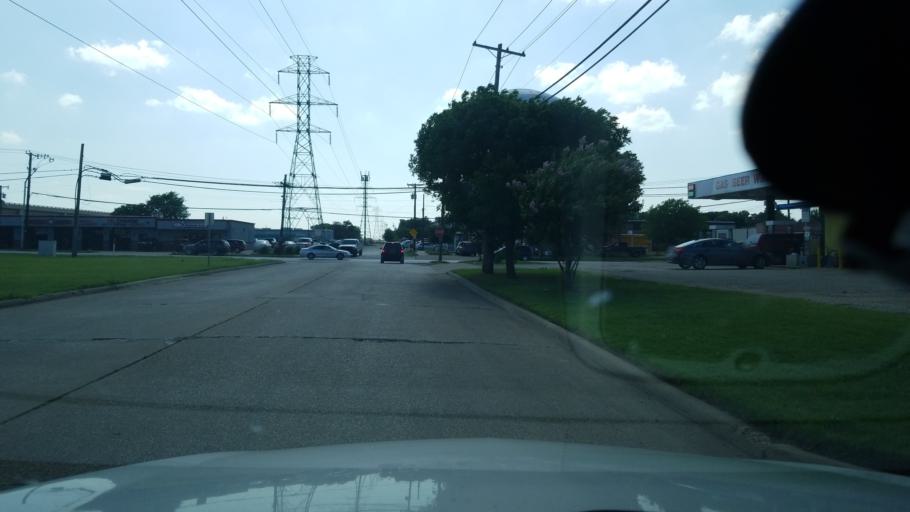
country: US
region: Texas
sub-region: Dallas County
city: Irving
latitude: 32.8162
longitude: -96.9756
